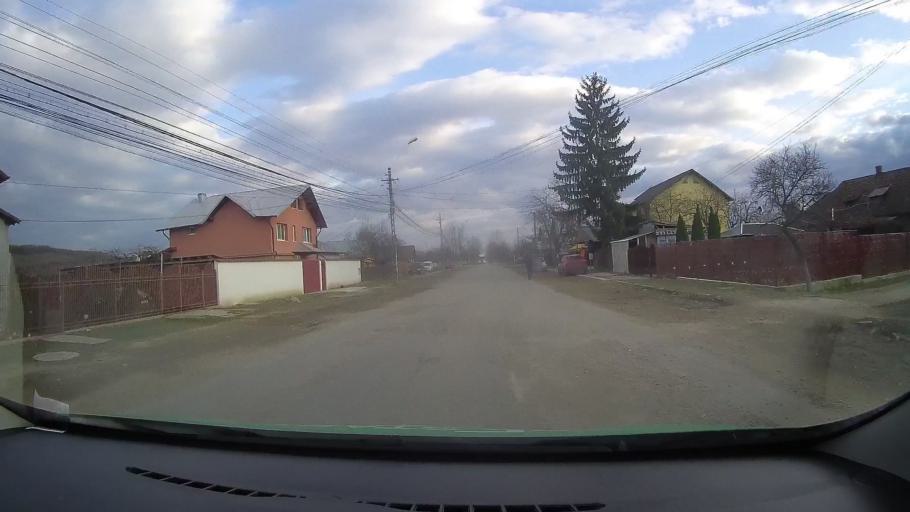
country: RO
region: Dambovita
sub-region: Municipiul Moreni
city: Moreni
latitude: 44.9676
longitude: 25.6532
